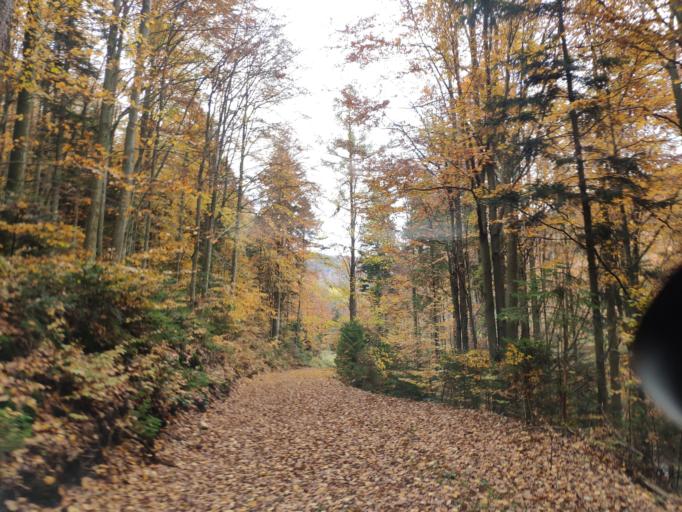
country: SK
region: Kosicky
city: Medzev
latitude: 48.7616
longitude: 20.9702
